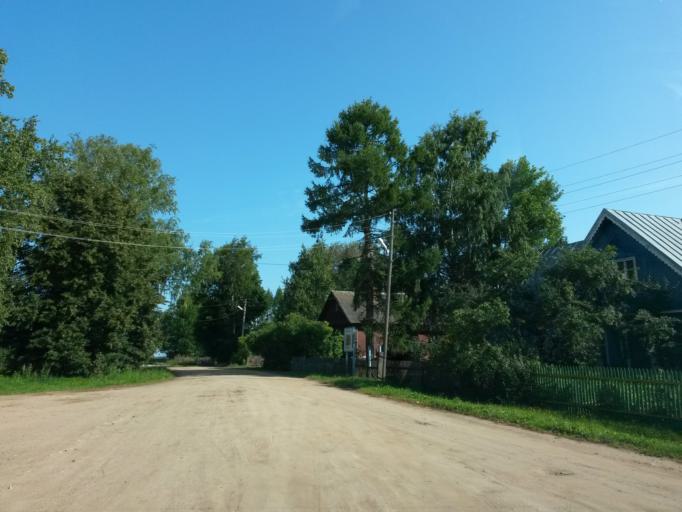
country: RU
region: Jaroslavl
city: Gavrilov-Yam
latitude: 57.3095
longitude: 39.9468
